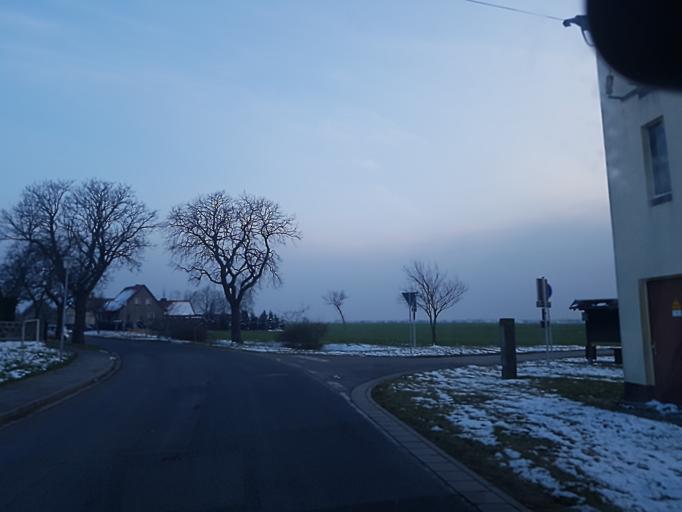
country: DE
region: Brandenburg
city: Muhlberg
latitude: 51.4574
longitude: 13.2583
